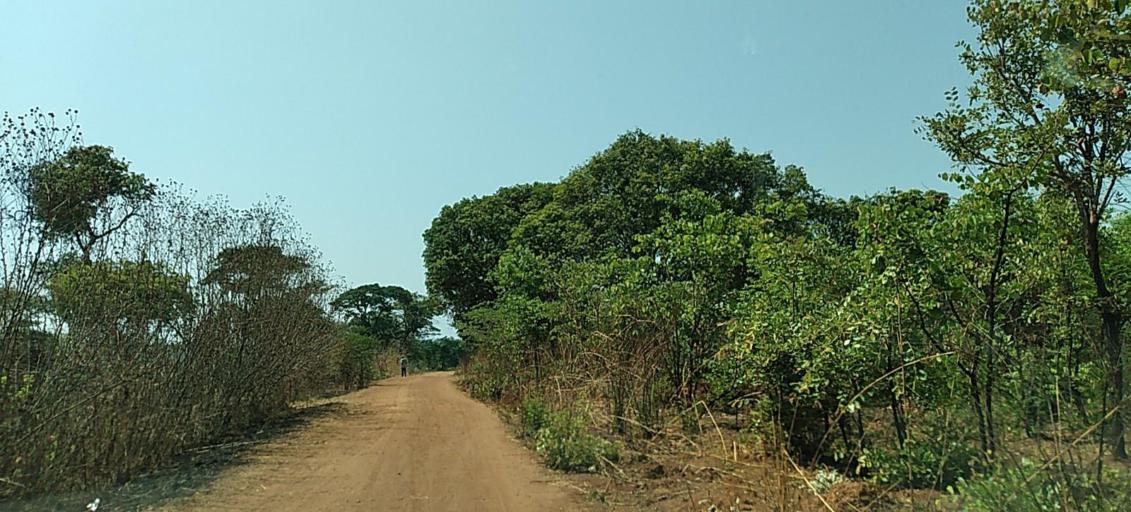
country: ZM
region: Copperbelt
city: Luanshya
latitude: -13.3449
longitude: 28.3928
